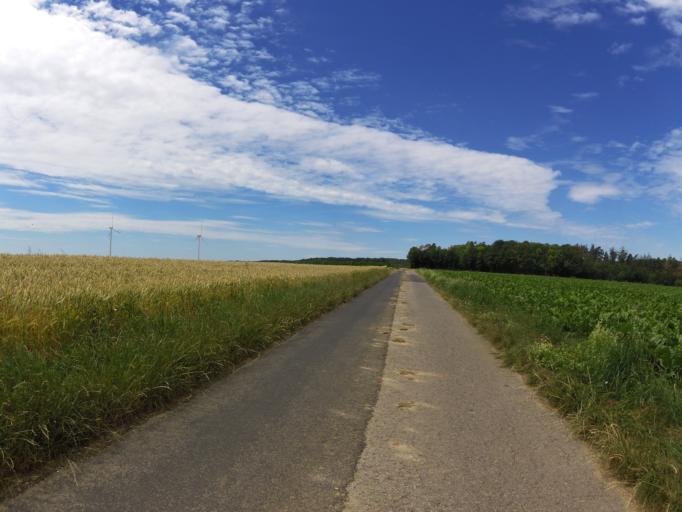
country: DE
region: Bavaria
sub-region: Regierungsbezirk Unterfranken
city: Geroldshausen
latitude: 49.7079
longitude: 9.8952
